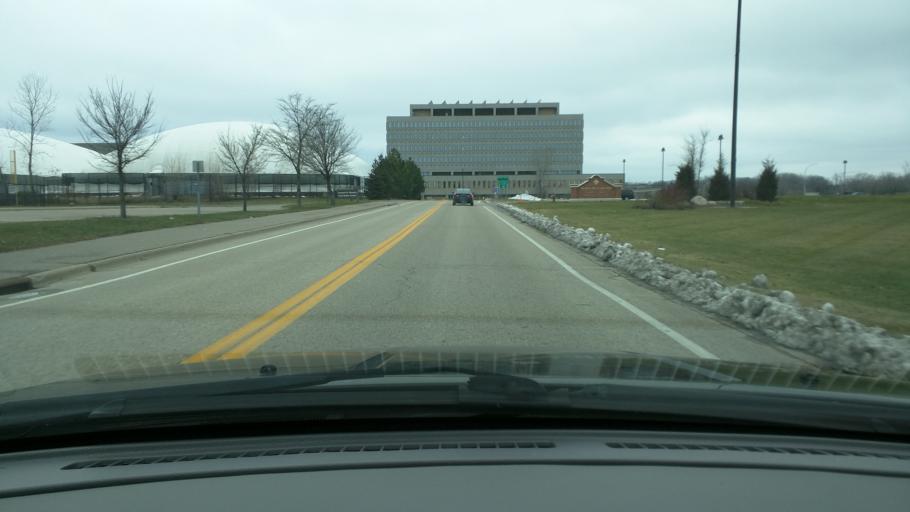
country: US
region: Minnesota
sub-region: Dakota County
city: Mendota Heights
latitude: 44.8925
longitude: -93.1919
